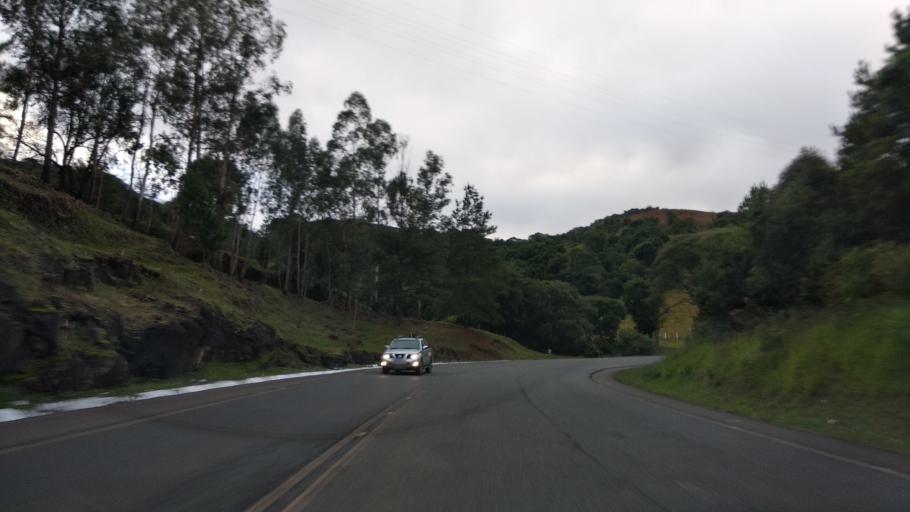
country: BR
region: Santa Catarina
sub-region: Campos Novos
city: Campos Novos
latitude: -27.4894
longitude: -50.9740
